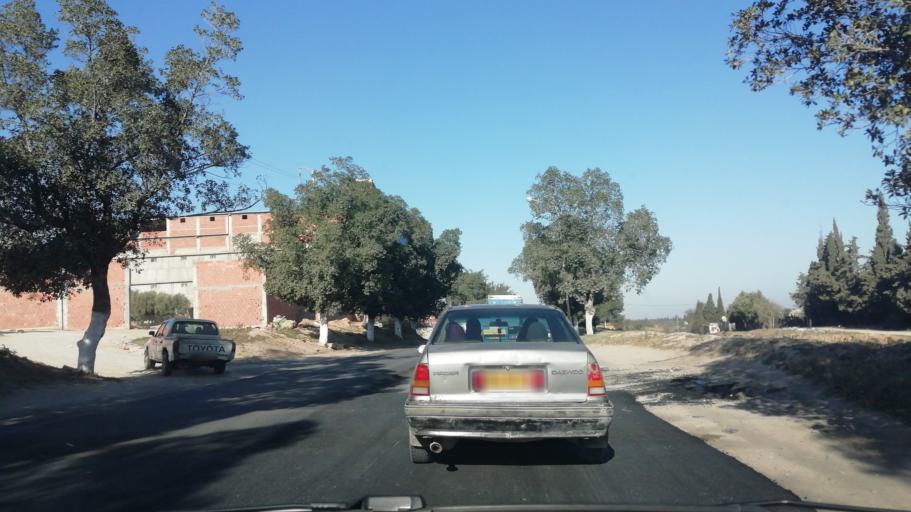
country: DZ
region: Mascara
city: Mascara
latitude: 35.5830
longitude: 0.0448
